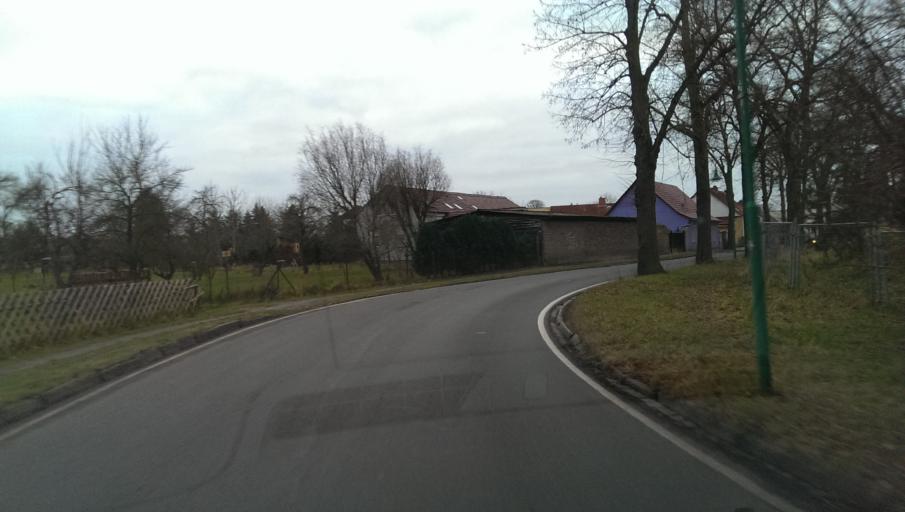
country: DE
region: Brandenburg
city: Zossen
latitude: 52.1596
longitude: 13.4598
